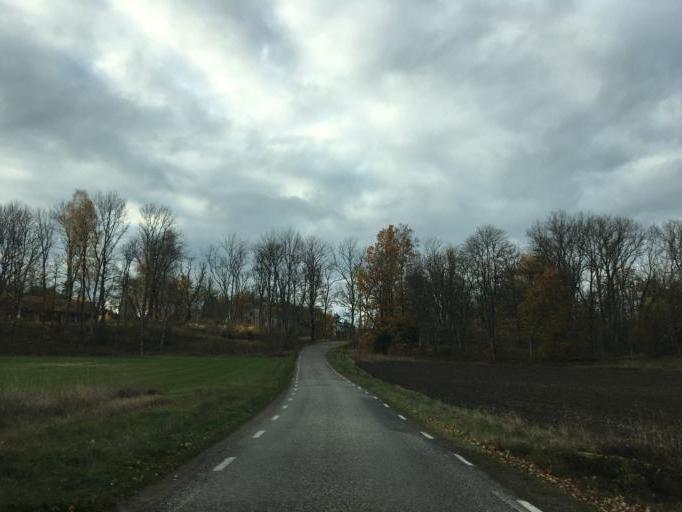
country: SE
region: Vaestmanland
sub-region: Vasteras
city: Vasteras
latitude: 59.5685
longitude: 16.4514
